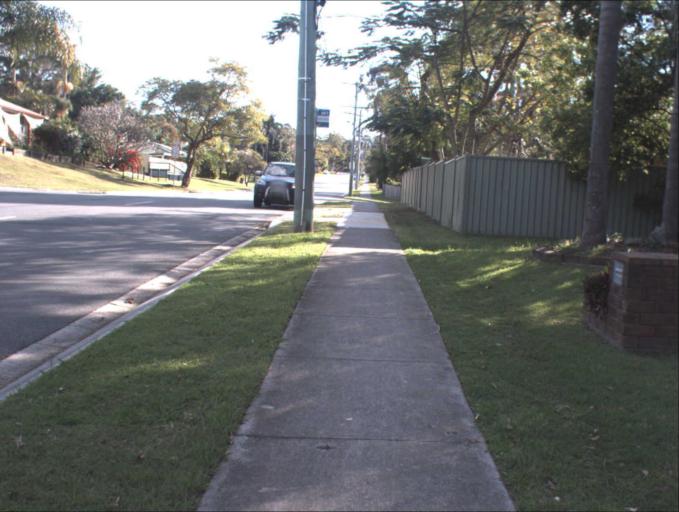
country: AU
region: Queensland
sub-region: Logan
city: Beenleigh
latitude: -27.7050
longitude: 153.1749
